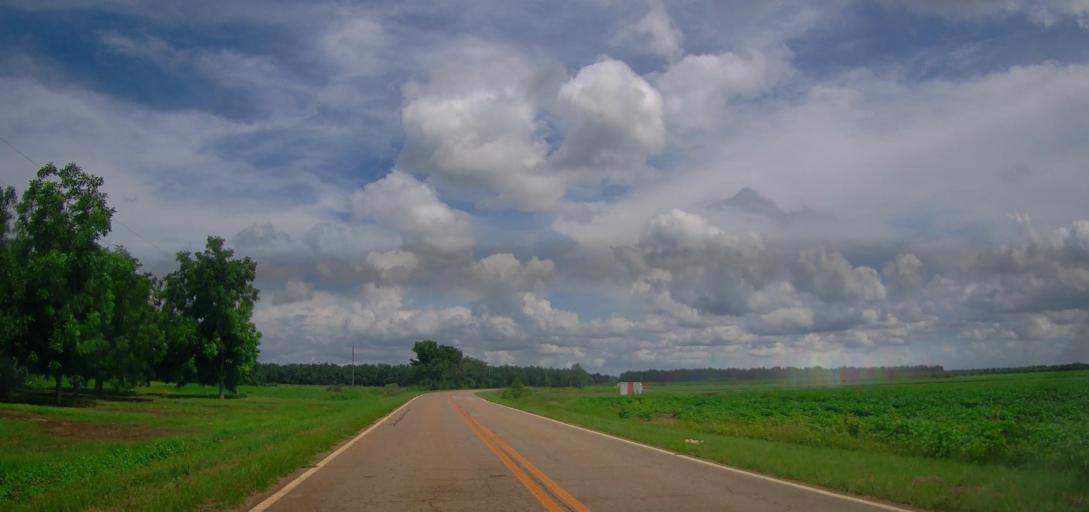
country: US
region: Georgia
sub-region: Houston County
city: Perry
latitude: 32.5216
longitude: -83.7697
